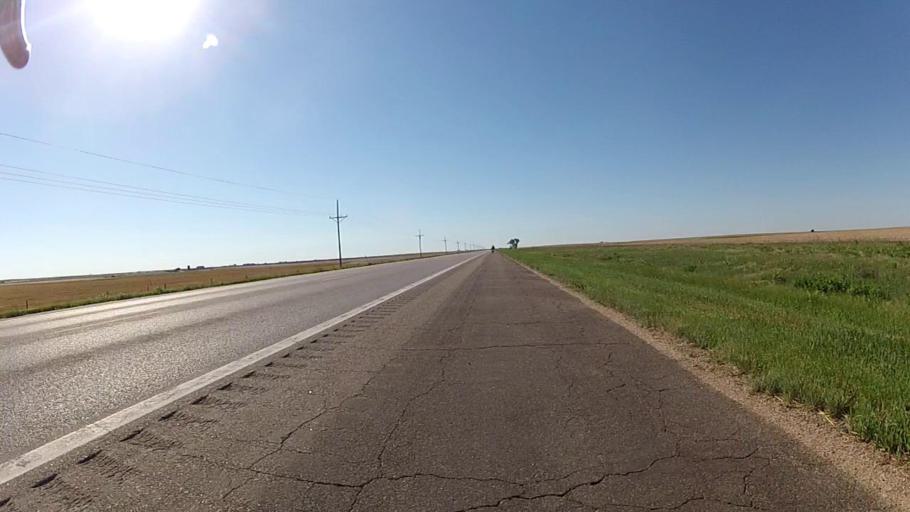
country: US
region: Kansas
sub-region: Ford County
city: Dodge City
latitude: 37.5967
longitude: -99.6963
